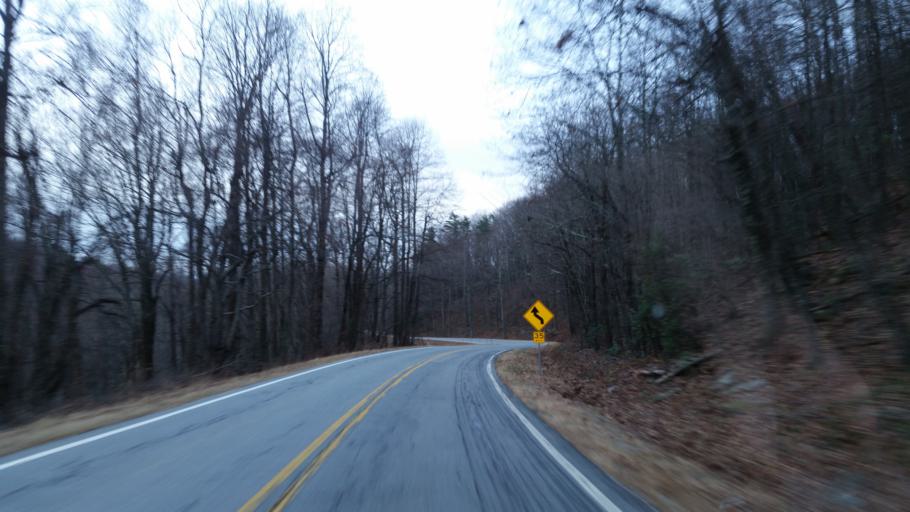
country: US
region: Georgia
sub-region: Pickens County
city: Jasper
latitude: 34.5457
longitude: -84.3264
